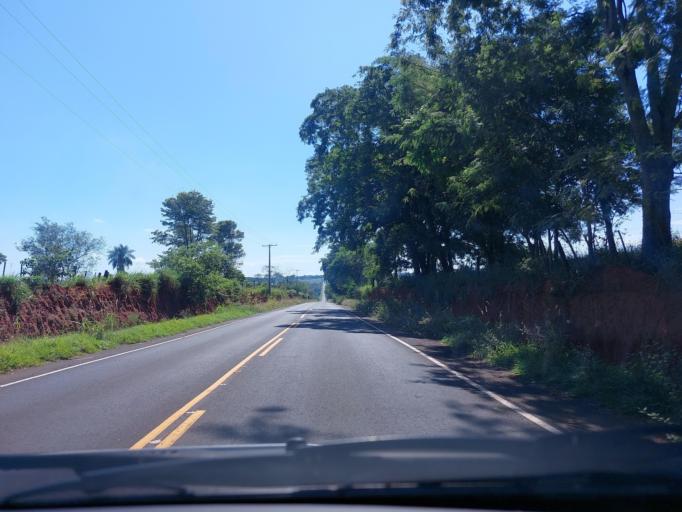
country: PY
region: San Pedro
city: Guayaybi
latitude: -24.5579
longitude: -56.5195
